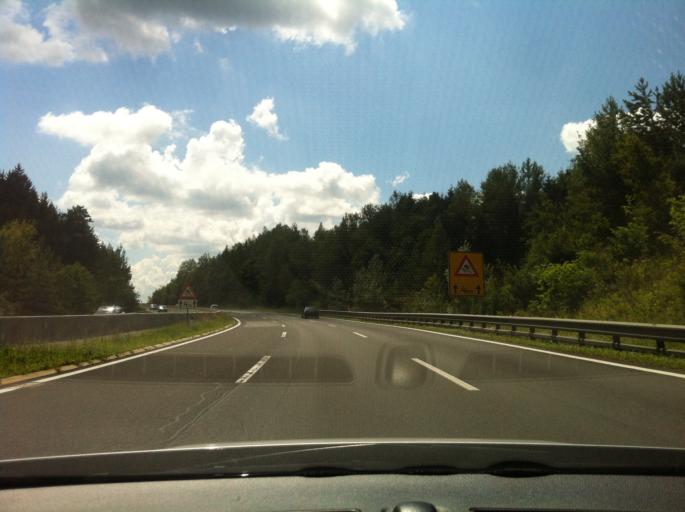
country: AT
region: Lower Austria
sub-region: Politischer Bezirk Neunkirchen
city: Thomasberg
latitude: 47.5515
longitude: 16.1300
